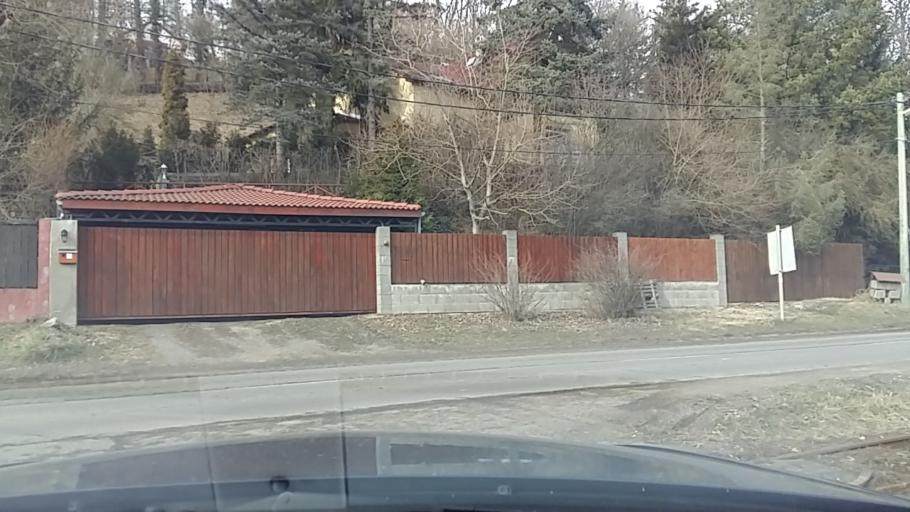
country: HU
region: Pest
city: Kismaros
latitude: 47.8378
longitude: 19.0058
